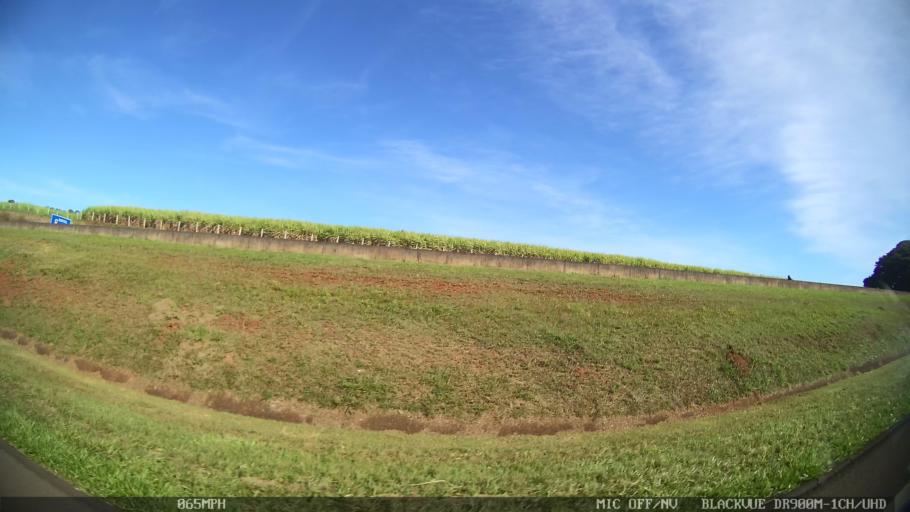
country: BR
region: Sao Paulo
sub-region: Araras
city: Araras
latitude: -22.3294
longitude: -47.3892
